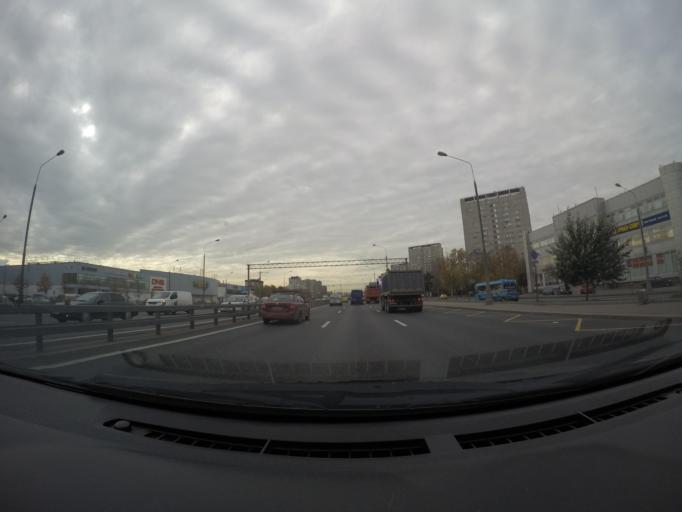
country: RU
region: Moscow
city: Yaroslavskiy
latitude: 55.8667
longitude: 37.7041
